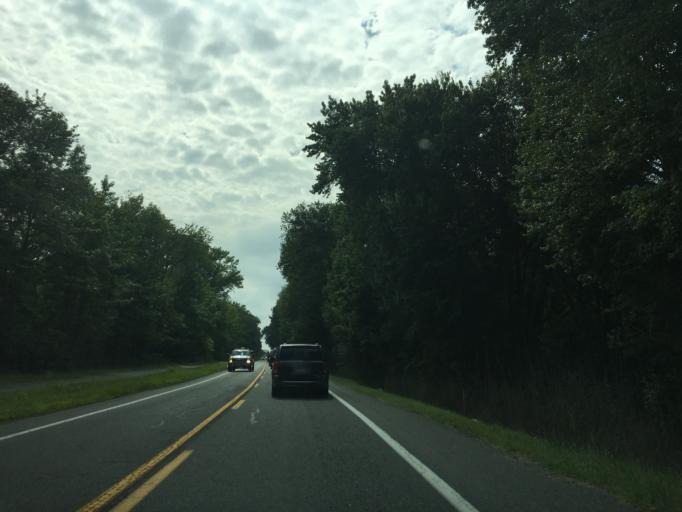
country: US
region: Delaware
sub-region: Sussex County
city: Ocean View
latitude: 38.5558
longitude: -75.0721
